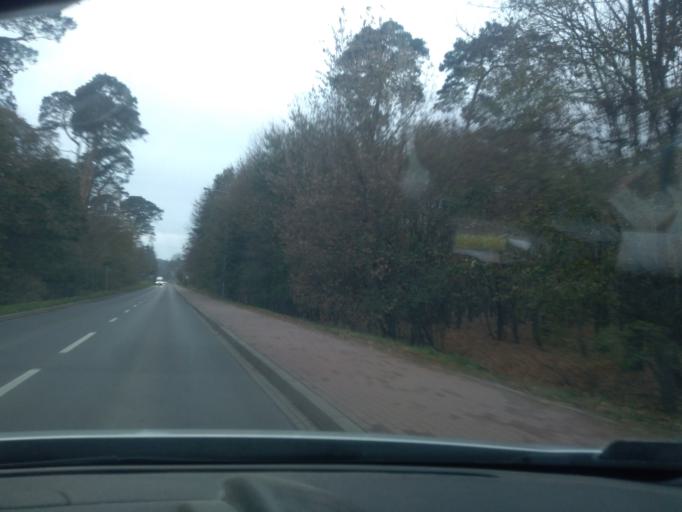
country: PL
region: Greater Poland Voivodeship
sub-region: Powiat poznanski
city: Murowana Goslina
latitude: 52.5409
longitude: 16.9710
